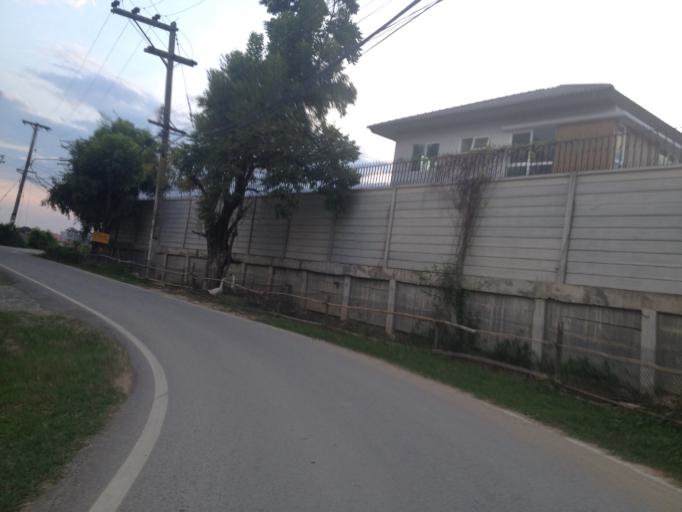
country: TH
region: Chiang Mai
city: Chiang Mai
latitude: 18.7563
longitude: 98.9586
